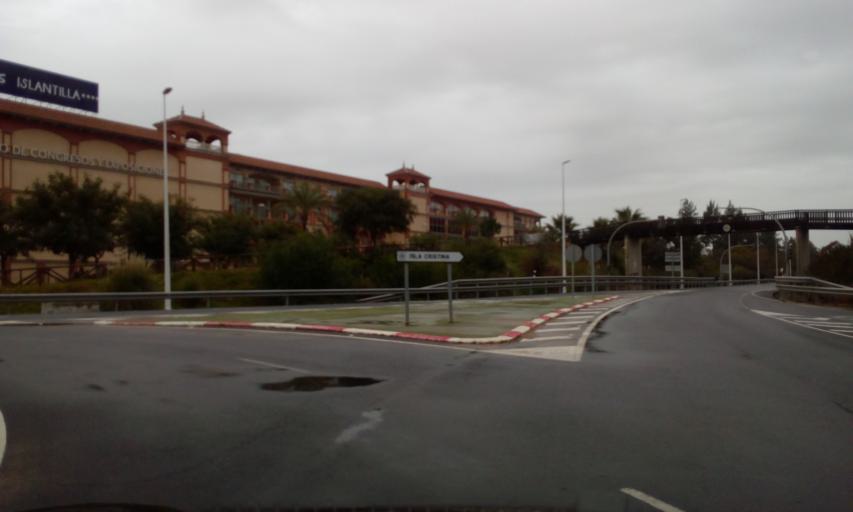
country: ES
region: Andalusia
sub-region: Provincia de Huelva
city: Lepe
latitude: 37.2088
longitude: -7.2303
